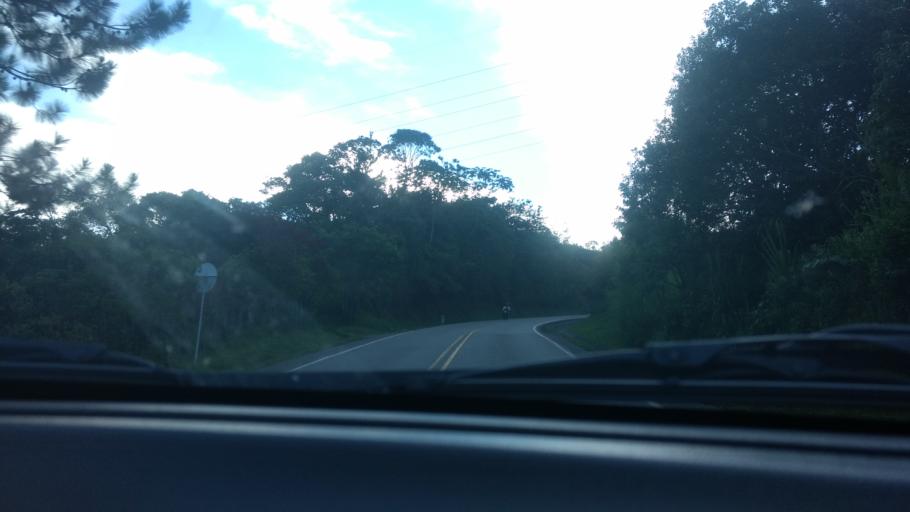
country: CO
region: Cauca
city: Rosas
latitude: 2.3356
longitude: -76.6921
